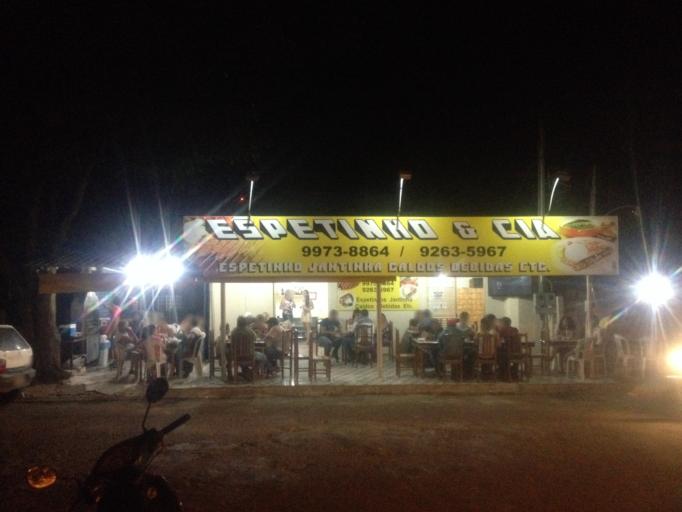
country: BR
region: Goias
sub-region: Mineiros
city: Mineiros
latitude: -17.5573
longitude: -52.5510
